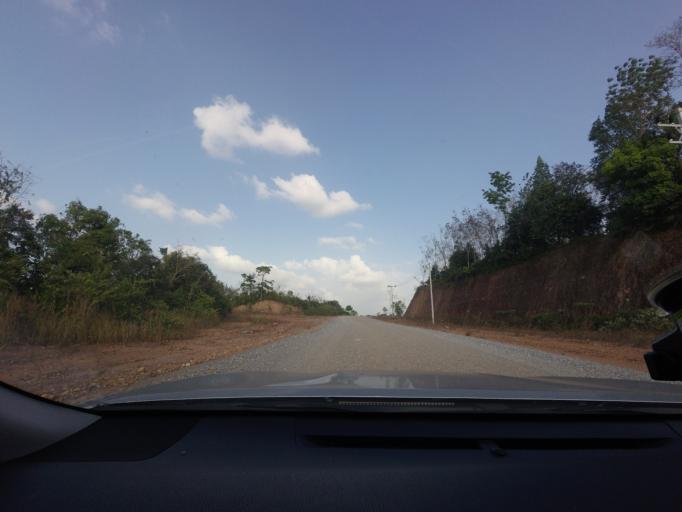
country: TH
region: Pattani
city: Mae Lan
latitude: 6.6056
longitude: 101.2454
